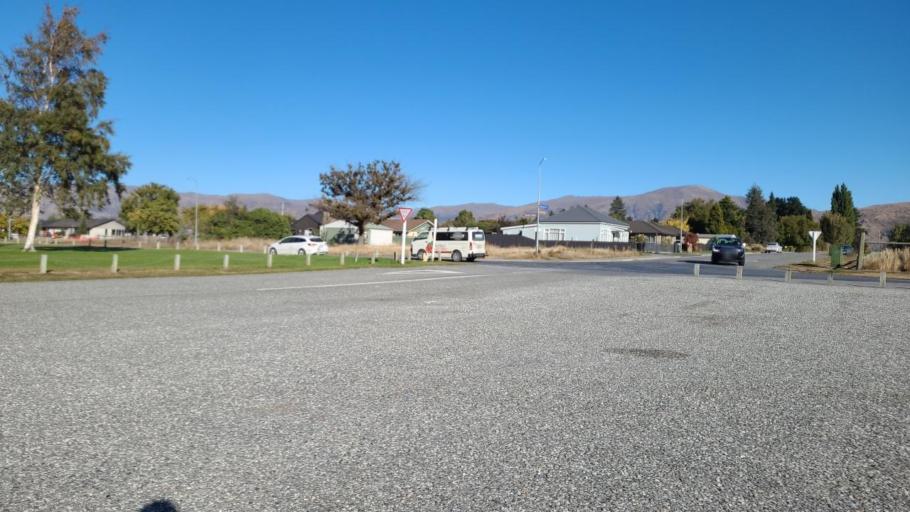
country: NZ
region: Otago
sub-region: Queenstown-Lakes District
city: Wanaka
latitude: -45.0423
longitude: 169.2146
